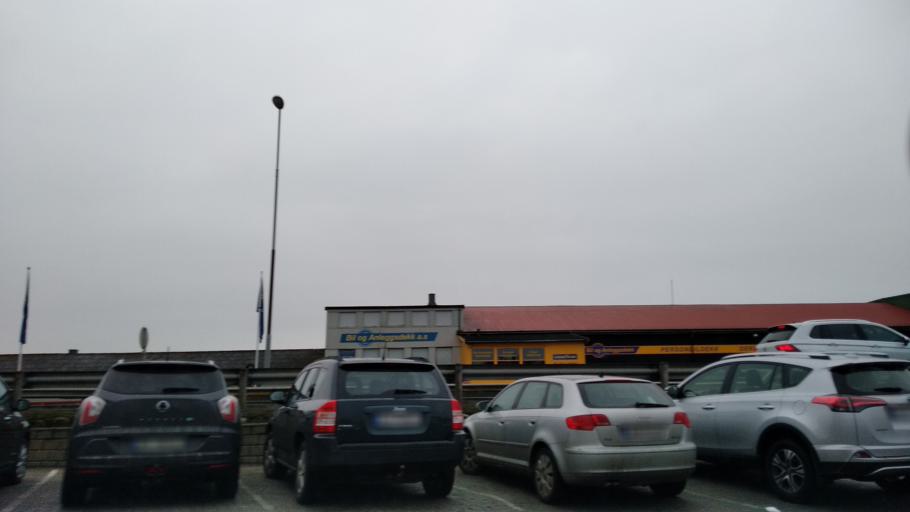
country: NO
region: Rogaland
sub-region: Randaberg
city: Randaberg
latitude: 58.9519
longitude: 5.6567
